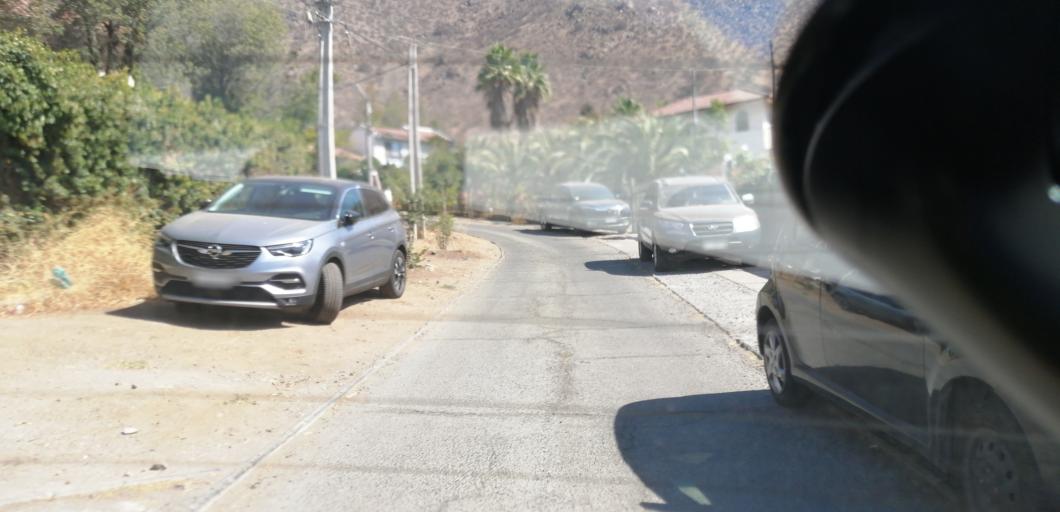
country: CL
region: Santiago Metropolitan
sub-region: Provincia de Santiago
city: Lo Prado
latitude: -33.4555
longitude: -70.8239
